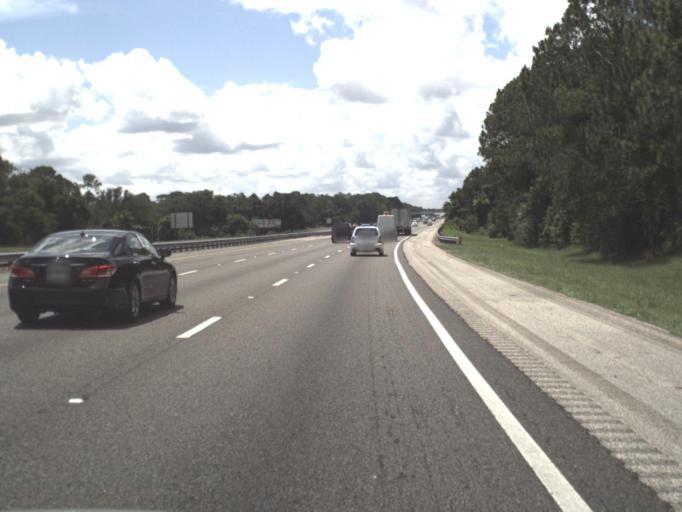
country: US
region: Florida
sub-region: Flagler County
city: Palm Coast
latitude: 29.6552
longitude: -81.2785
